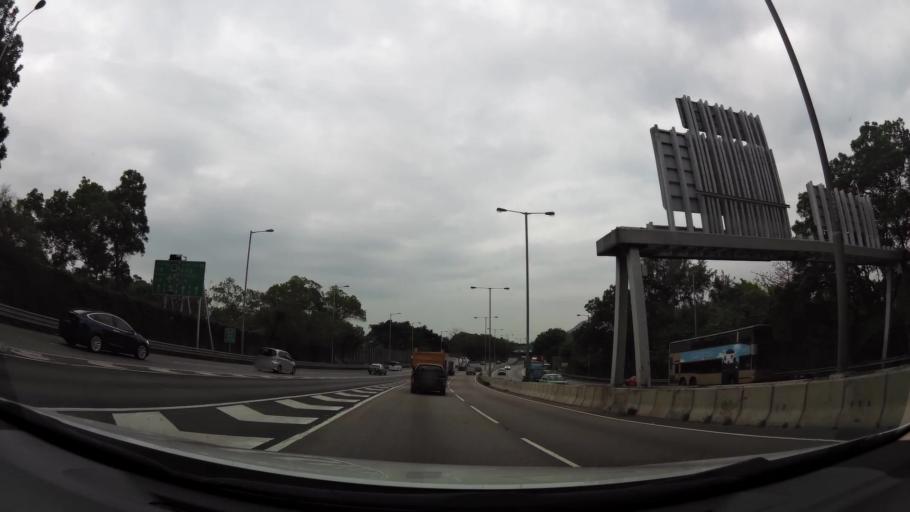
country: HK
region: Yuen Long
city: Yuen Long Kau Hui
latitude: 22.4468
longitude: 114.0397
